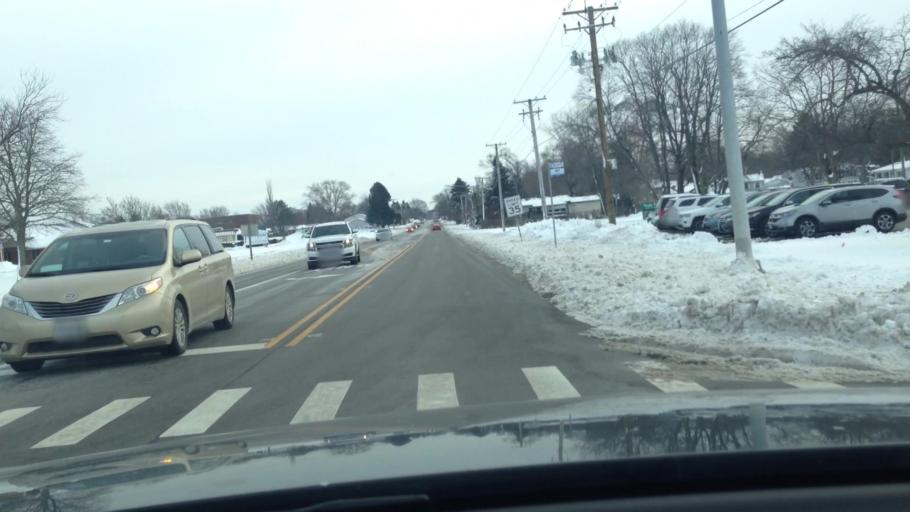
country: US
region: Illinois
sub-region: McHenry County
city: Woodstock
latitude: 42.3397
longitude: -88.4433
